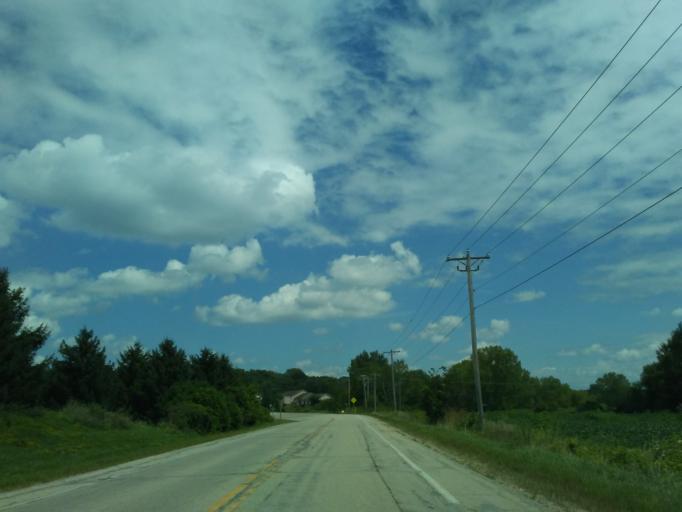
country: US
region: Wisconsin
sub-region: Dane County
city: Verona
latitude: 43.0130
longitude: -89.5602
